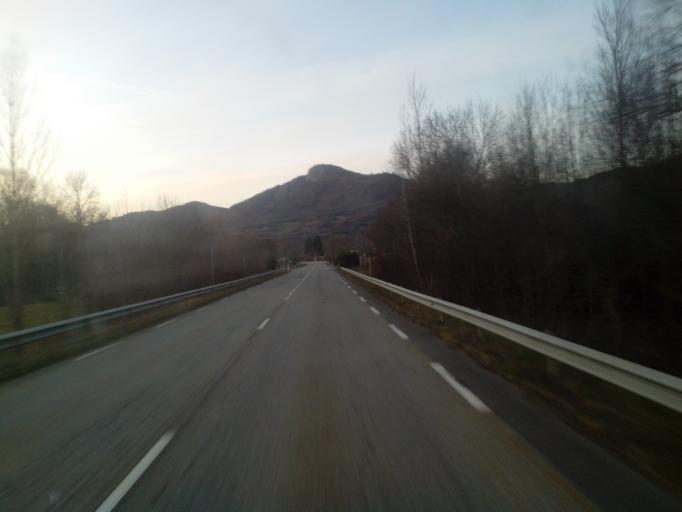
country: FR
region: Midi-Pyrenees
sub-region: Departement de l'Ariege
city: Saint-Paul-de-Jarrat
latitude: 42.9300
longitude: 1.7349
